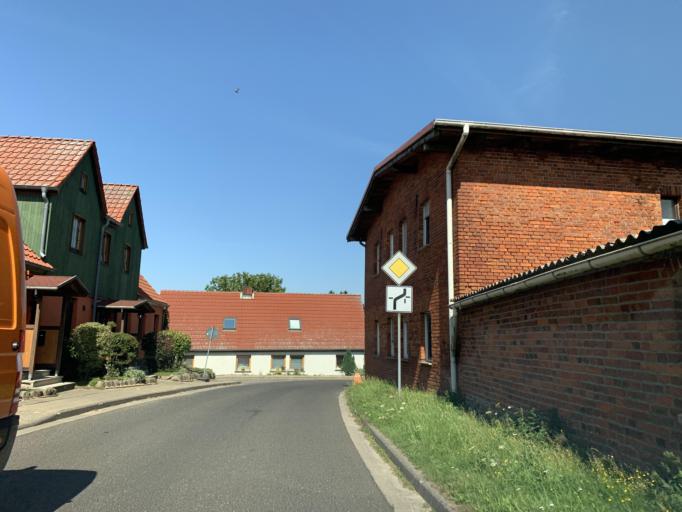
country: DE
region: Mecklenburg-Vorpommern
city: Loitz
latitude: 53.3384
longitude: 13.3842
